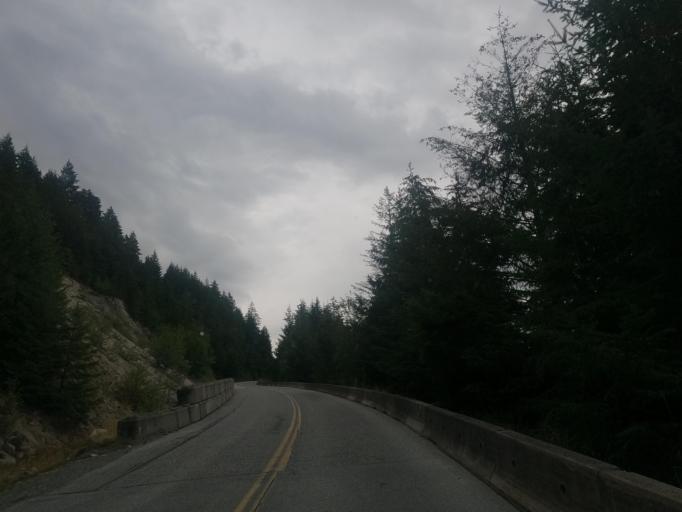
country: CA
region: British Columbia
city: Pemberton
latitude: 50.3021
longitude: -122.5884
